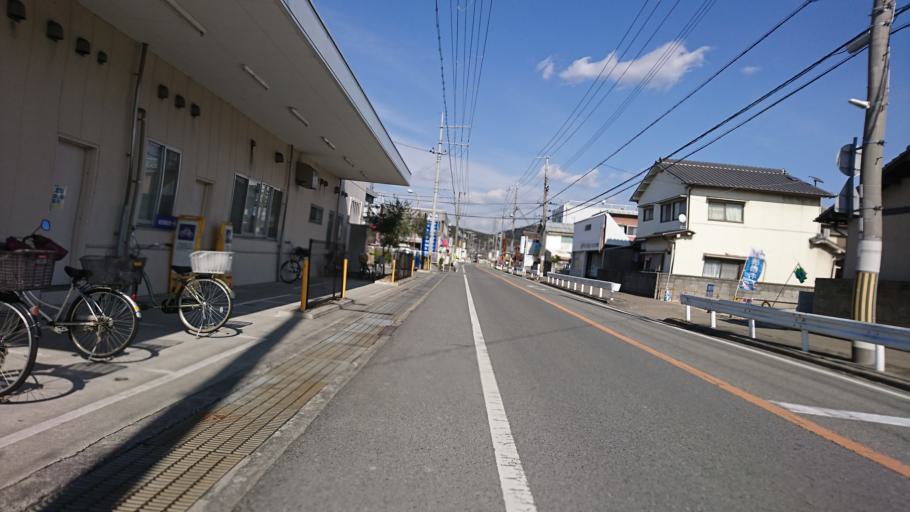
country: JP
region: Hyogo
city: Kakogawacho-honmachi
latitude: 34.7913
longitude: 134.8241
